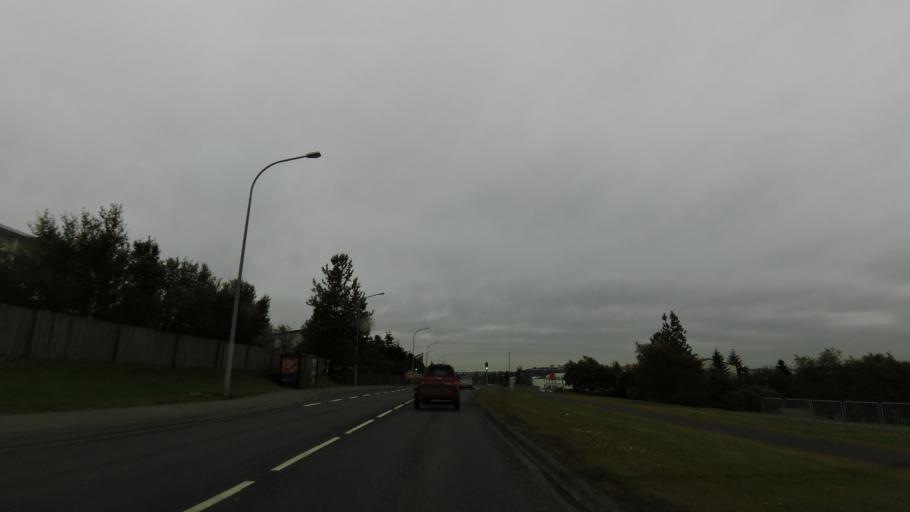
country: IS
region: Capital Region
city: Reykjavik
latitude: 64.1214
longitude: -21.8665
